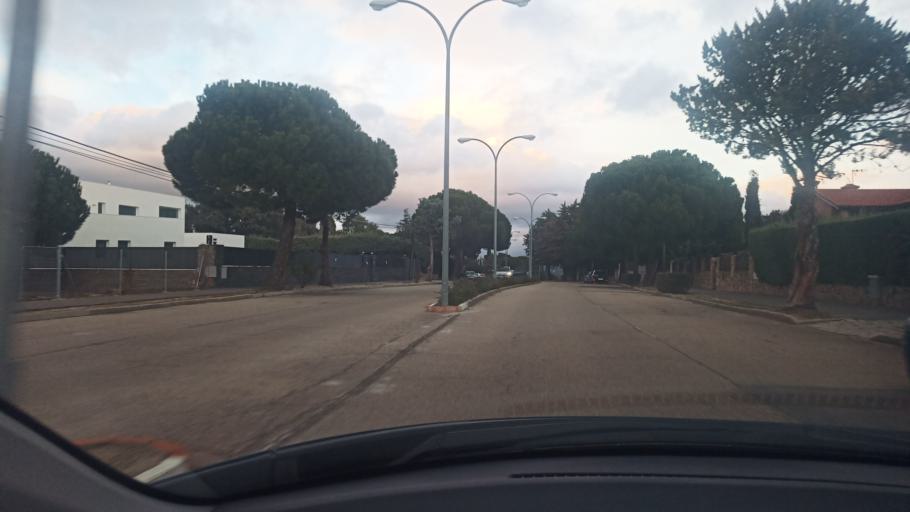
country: ES
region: Madrid
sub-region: Provincia de Madrid
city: Valdemorillo
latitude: 40.5342
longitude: -4.0928
